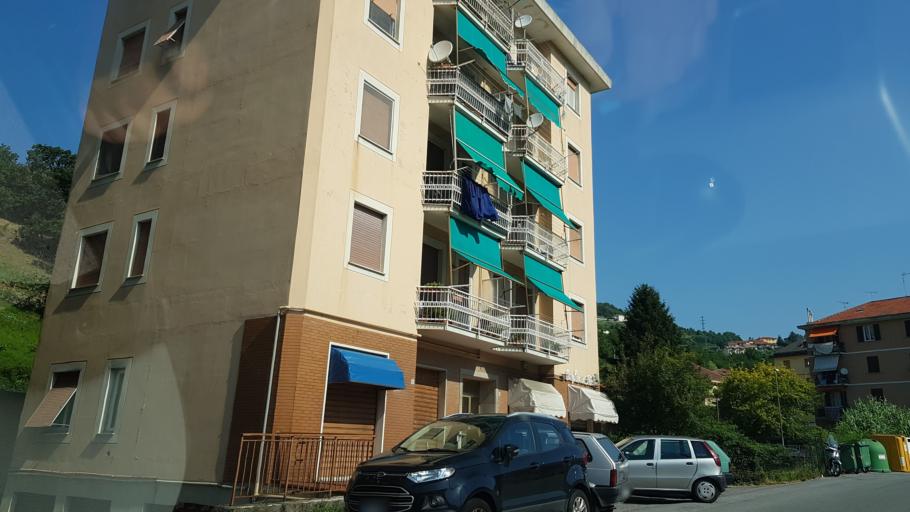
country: IT
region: Liguria
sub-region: Provincia di Genova
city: Pedemonte
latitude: 44.4953
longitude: 8.9205
